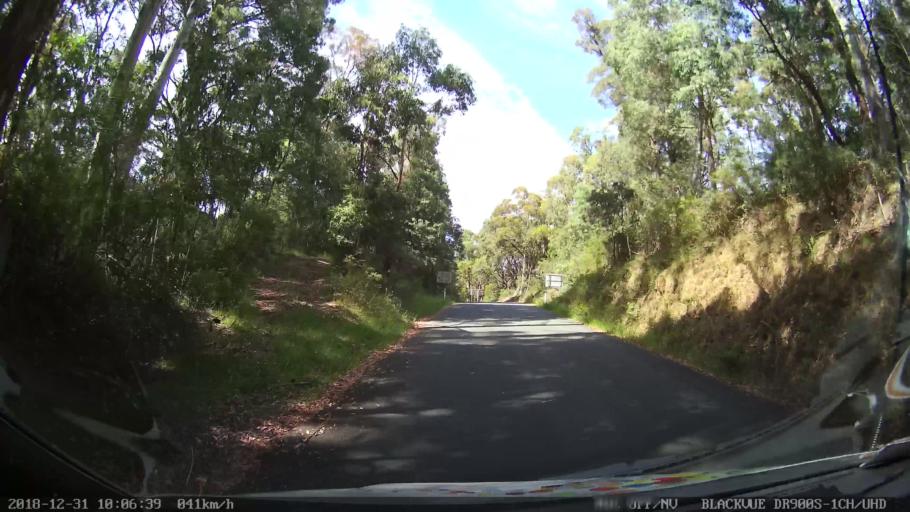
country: AU
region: New South Wales
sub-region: Snowy River
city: Jindabyne
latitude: -36.5295
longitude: 148.1873
